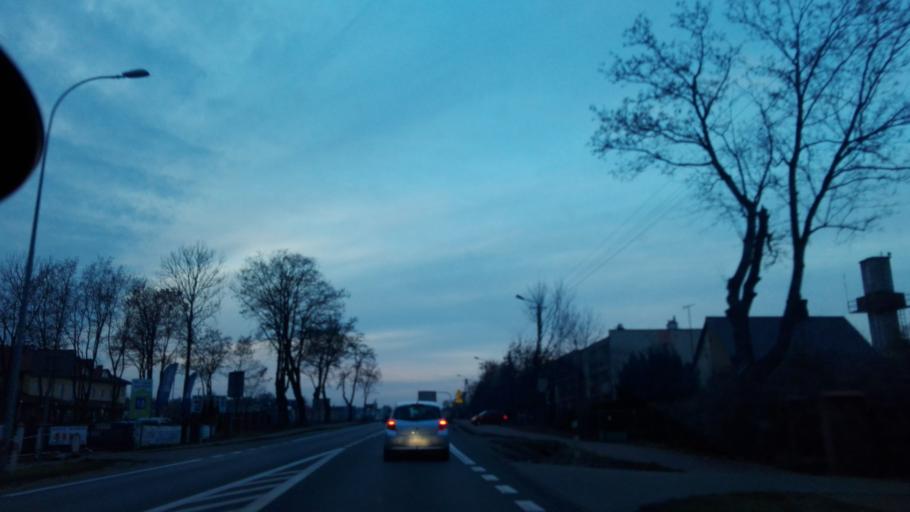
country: PL
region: Masovian Voivodeship
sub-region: Siedlce
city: Siedlce
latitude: 52.1727
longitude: 22.2142
